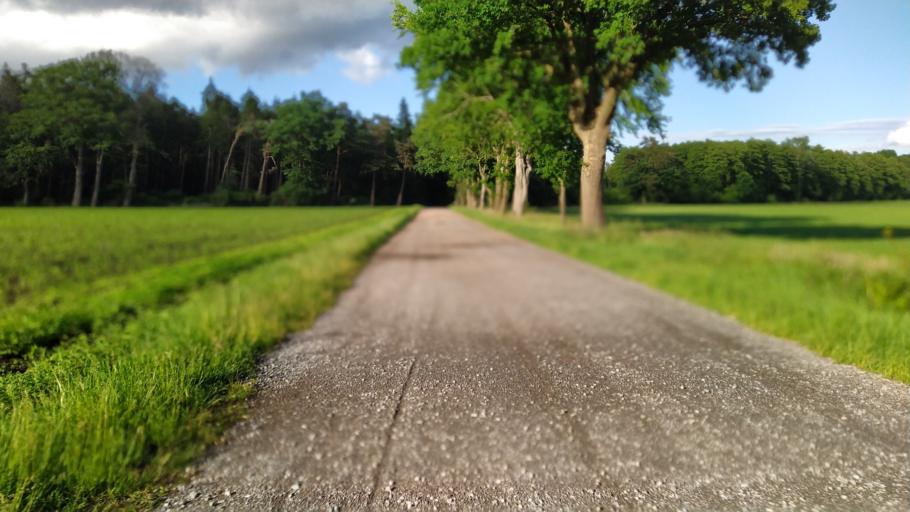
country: DE
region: Lower Saxony
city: Farven
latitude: 53.4490
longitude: 9.3252
